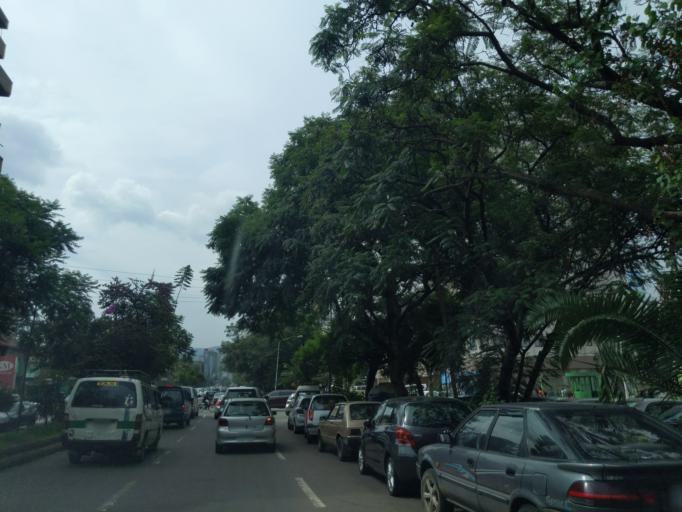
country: ET
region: Adis Abeba
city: Addis Ababa
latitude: 9.0133
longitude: 38.7530
